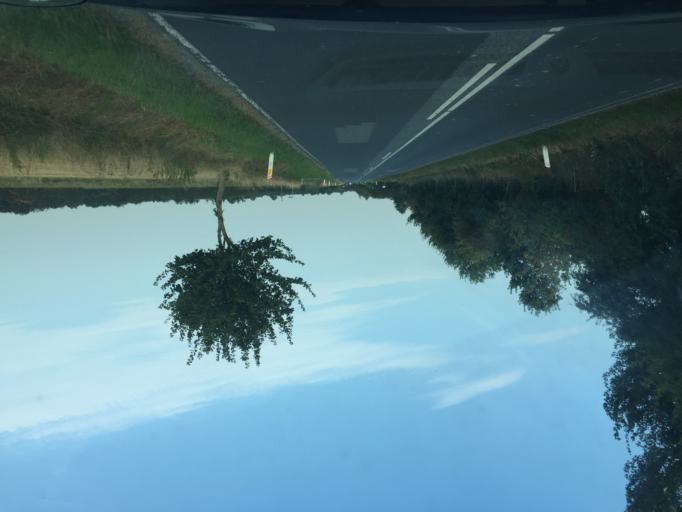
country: DK
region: South Denmark
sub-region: Kerteminde Kommune
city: Langeskov
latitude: 55.2884
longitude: 10.5556
